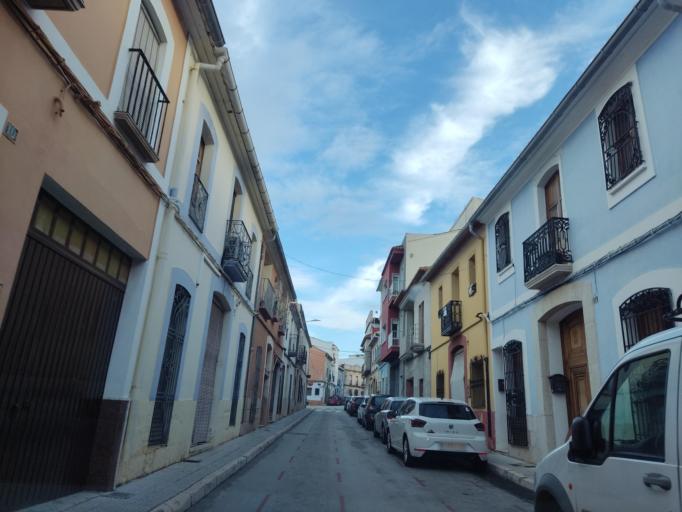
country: ES
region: Valencia
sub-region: Provincia de Alicante
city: Pedreguer
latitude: 38.7953
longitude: 0.0325
